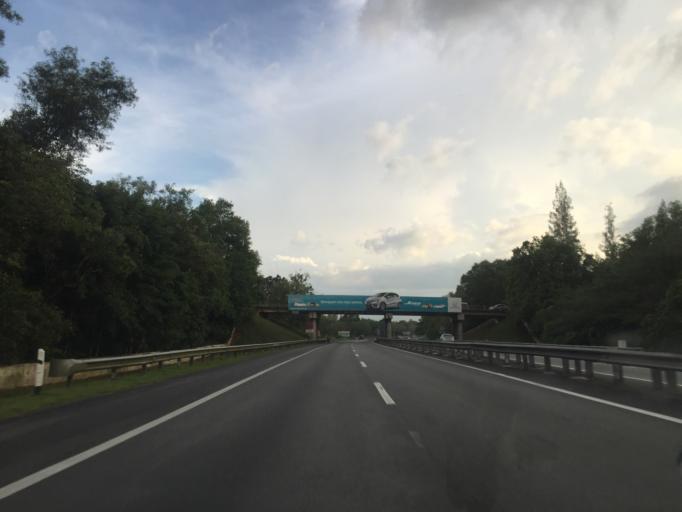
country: MY
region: Kedah
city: Bedong
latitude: 5.7315
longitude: 100.5218
